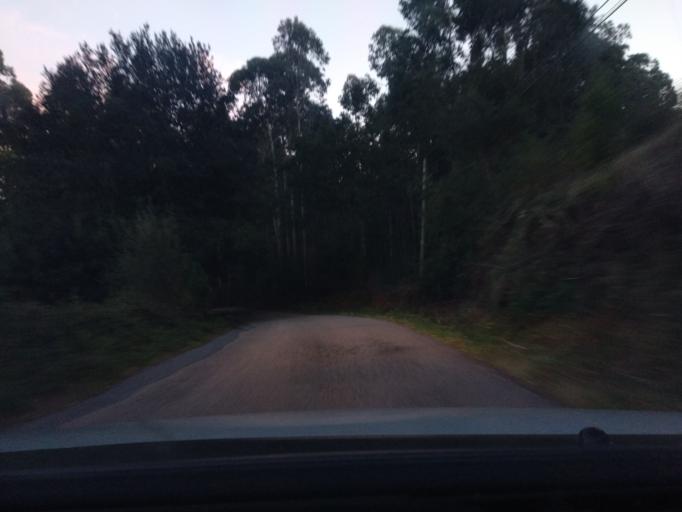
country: ES
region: Galicia
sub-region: Provincia de Pontevedra
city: Moana
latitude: 42.3005
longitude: -8.6975
